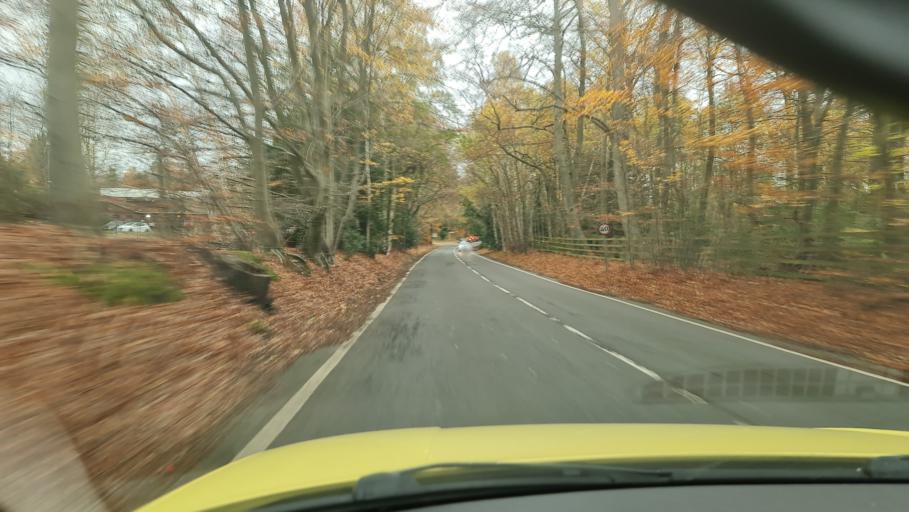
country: GB
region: England
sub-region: Bracknell Forest
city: Sandhurst
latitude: 51.3245
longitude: -0.7800
